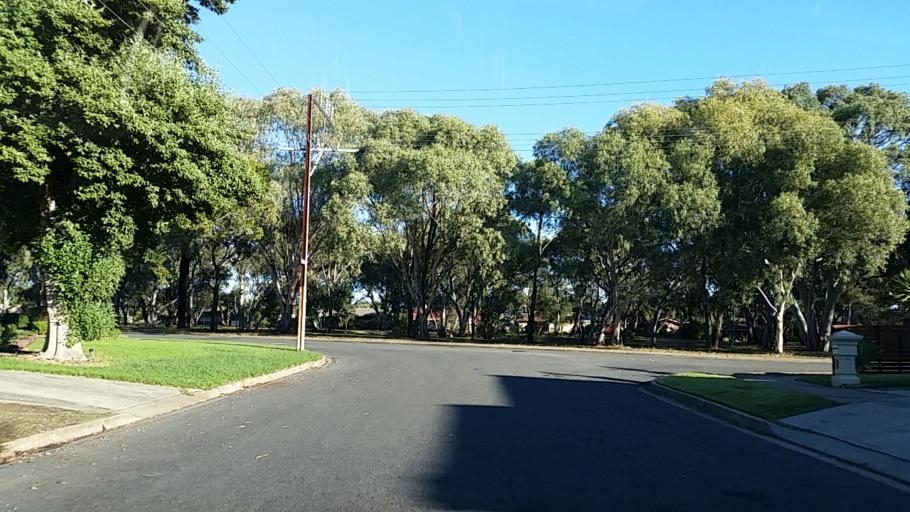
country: AU
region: South Australia
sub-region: Onkaparinga
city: Morphett Vale
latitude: -35.1211
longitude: 138.5341
